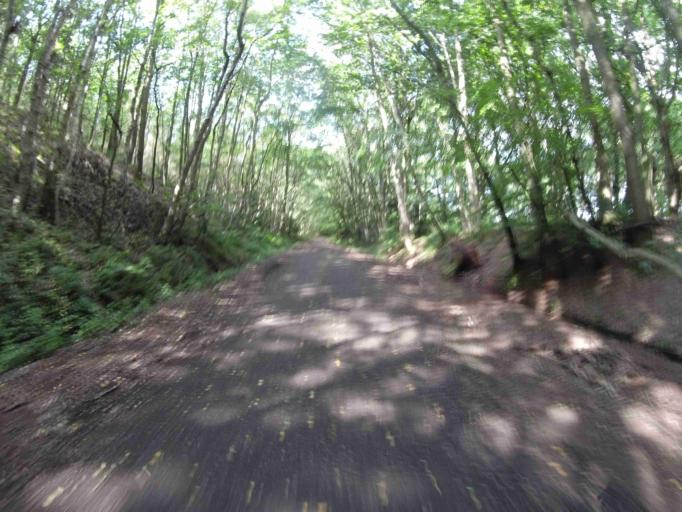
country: GB
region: England
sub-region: Devon
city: Budleigh Salterton
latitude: 50.6354
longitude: -3.3516
